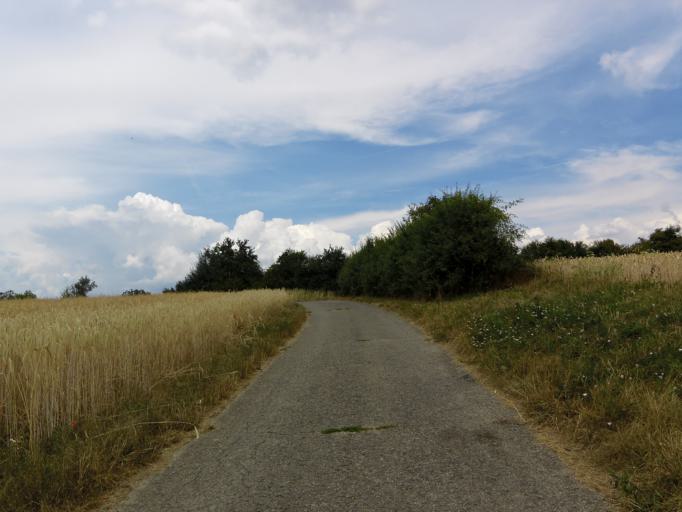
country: DE
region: Bavaria
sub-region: Regierungsbezirk Unterfranken
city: Gerbrunn
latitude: 49.7745
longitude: 9.9895
